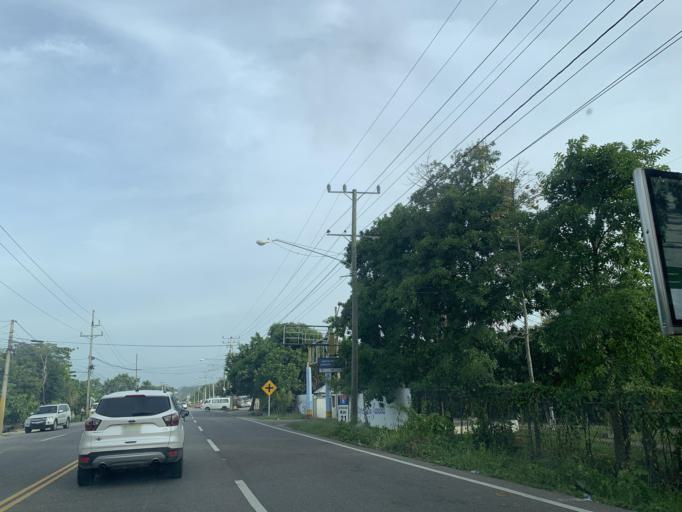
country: DO
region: Puerto Plata
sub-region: Puerto Plata
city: Puerto Plata
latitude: 19.7545
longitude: -70.6426
